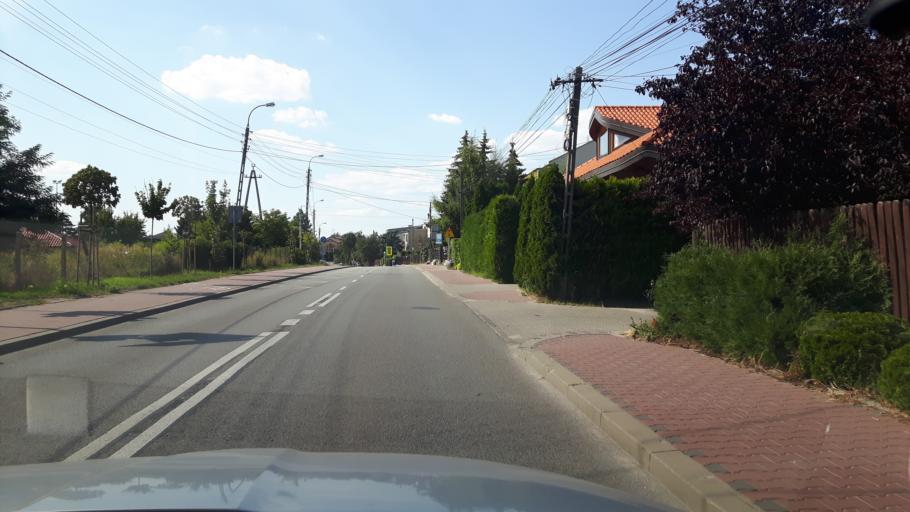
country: PL
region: Masovian Voivodeship
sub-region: Powiat pruszkowski
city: Raszyn
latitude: 52.1594
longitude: 20.9192
